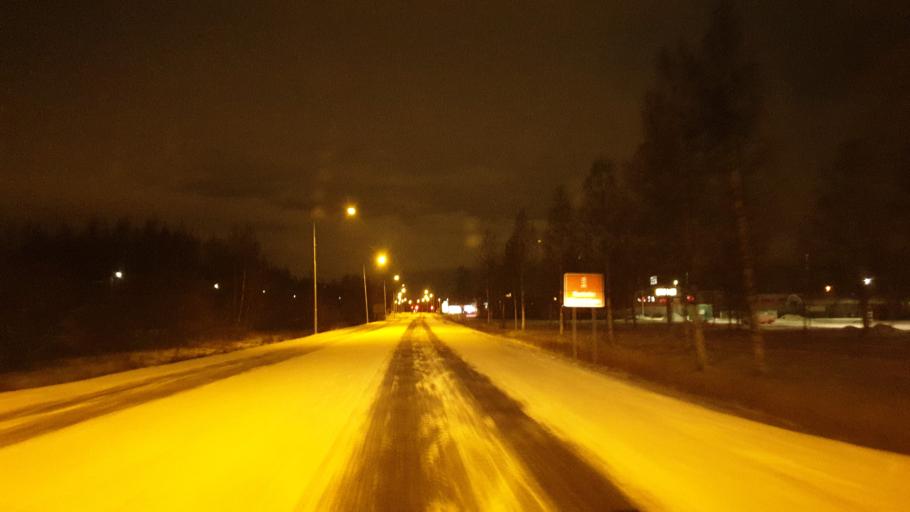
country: FI
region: Northern Ostrobothnia
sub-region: Oulu
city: Kempele
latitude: 64.9576
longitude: 25.5043
